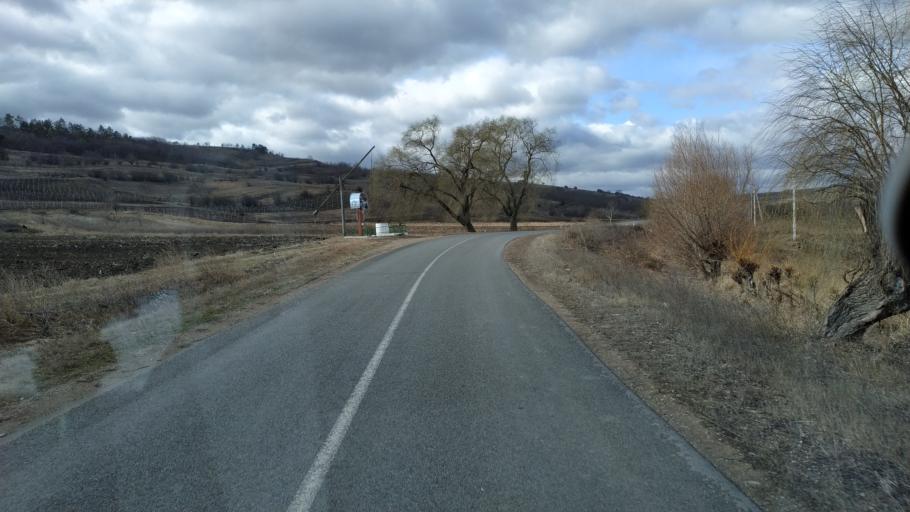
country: MD
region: Stinga Nistrului
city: Bucovat
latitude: 47.1425
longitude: 28.3760
